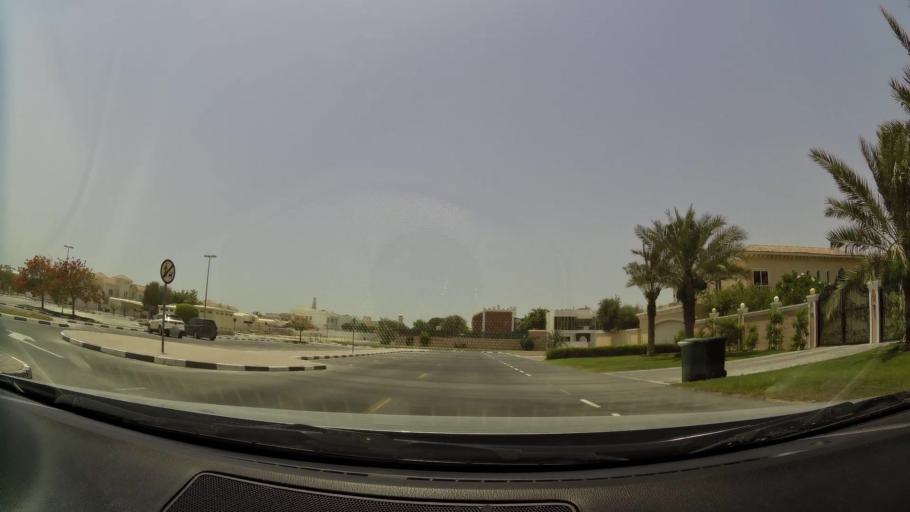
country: AE
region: Dubai
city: Dubai
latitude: 25.1660
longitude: 55.2178
